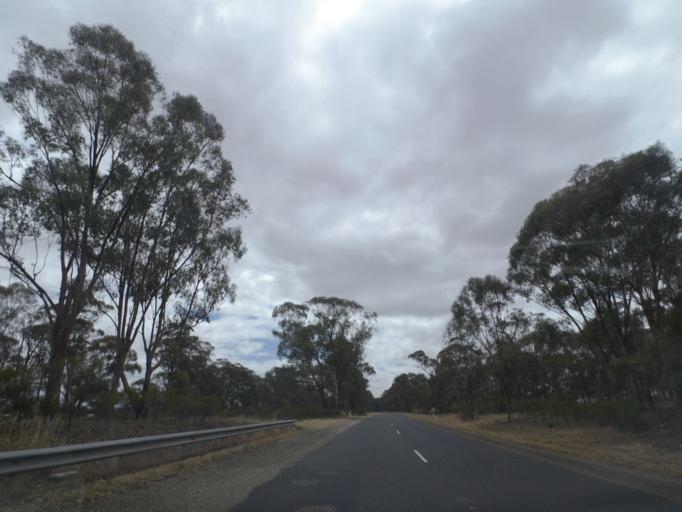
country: AU
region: Victoria
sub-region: Murrindindi
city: Kinglake West
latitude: -36.9829
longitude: 145.1604
